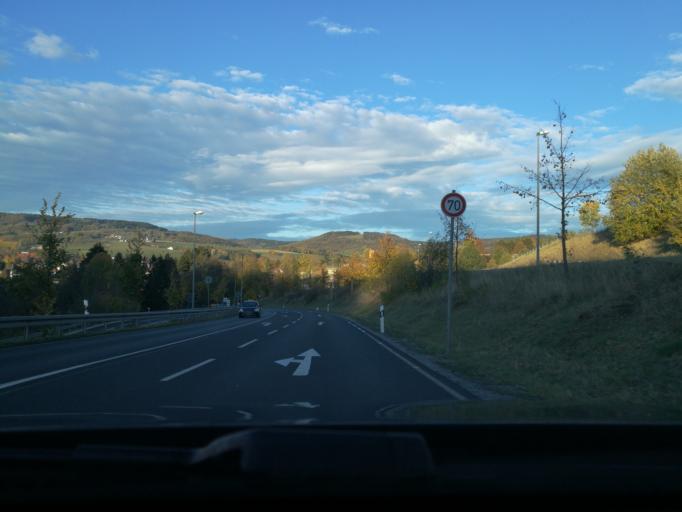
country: DE
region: Hesse
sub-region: Regierungsbezirk Kassel
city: Gersfeld
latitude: 50.4440
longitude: 9.9190
